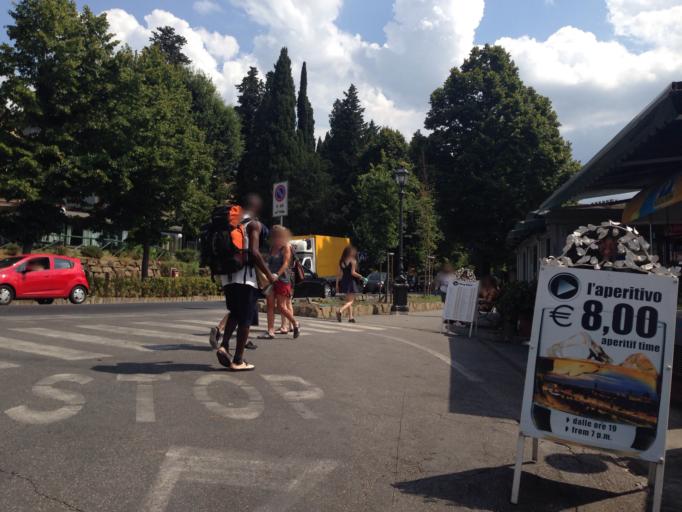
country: IT
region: Tuscany
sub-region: Province of Florence
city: Florence
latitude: 43.7622
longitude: 11.2641
